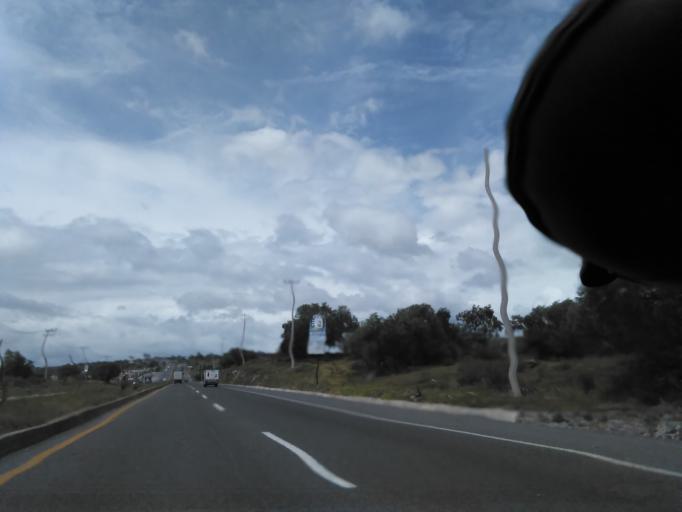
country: MX
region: Hidalgo
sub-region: Atotonilco de Tula
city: Paseos de la Pradera
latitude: 19.9204
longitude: -99.2381
